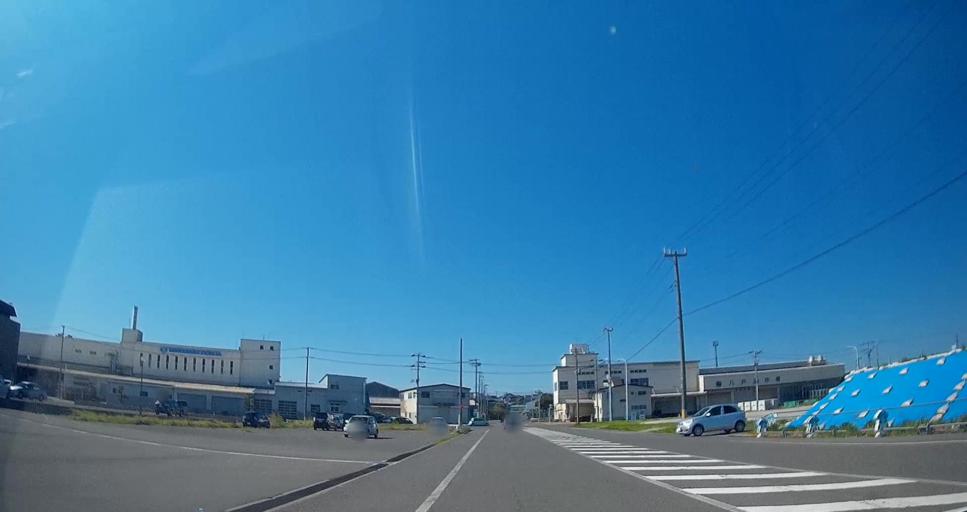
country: JP
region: Aomori
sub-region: Hachinohe Shi
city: Uchimaru
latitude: 40.5274
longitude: 141.5351
